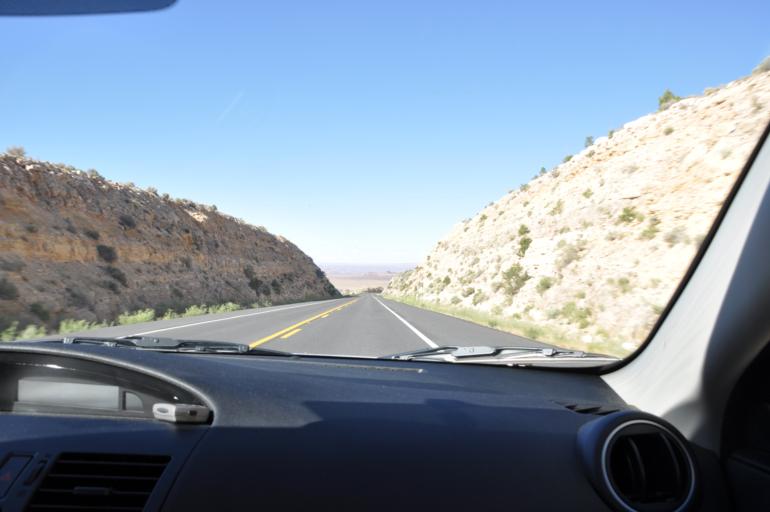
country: US
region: Arizona
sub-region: Coconino County
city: Grand Canyon
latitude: 35.9336
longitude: -111.7079
